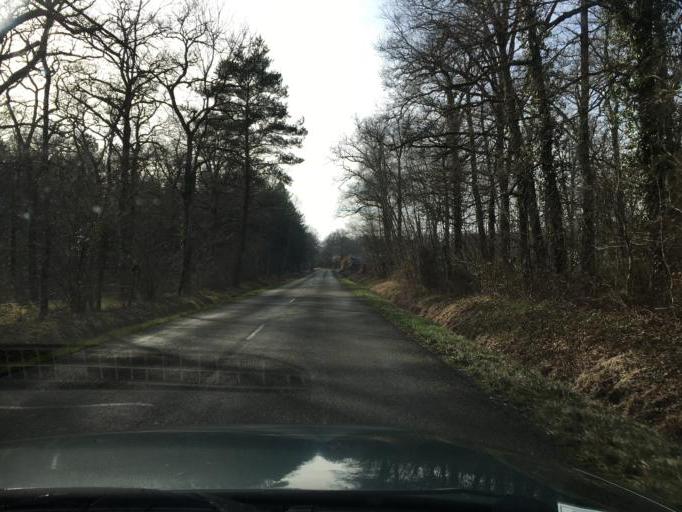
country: FR
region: Centre
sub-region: Departement du Loiret
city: Jouy-le-Potier
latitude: 47.7061
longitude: 1.8475
